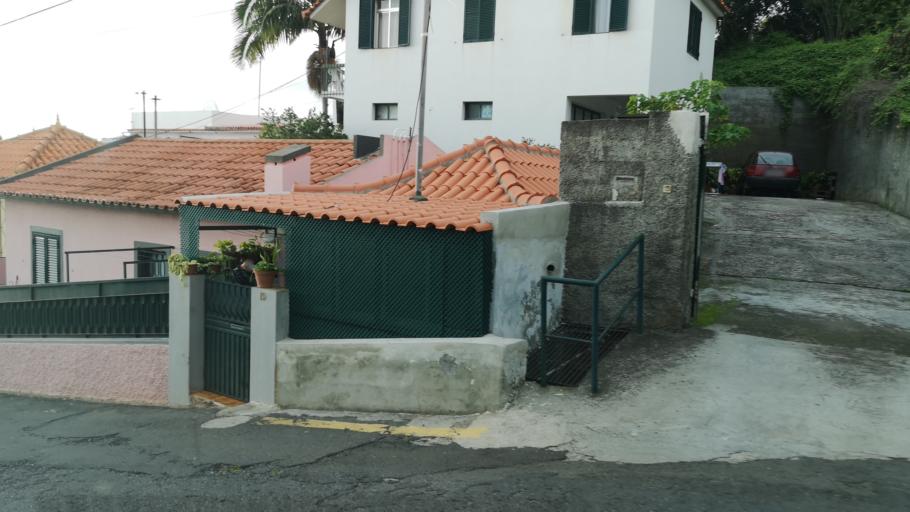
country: PT
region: Madeira
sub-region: Funchal
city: Nossa Senhora do Monte
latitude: 32.6563
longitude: -16.8919
